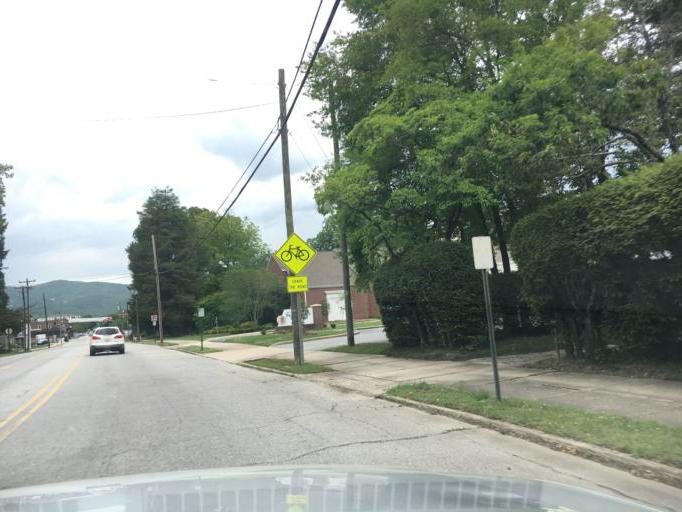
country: US
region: North Carolina
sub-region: Transylvania County
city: Brevard
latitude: 35.2317
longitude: -82.7298
